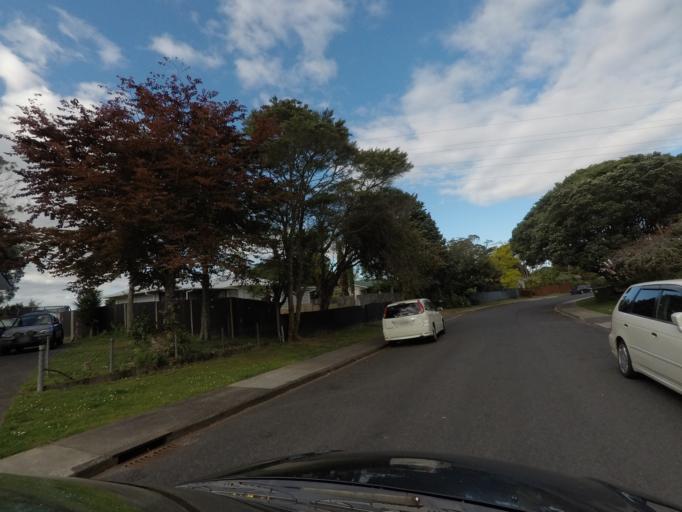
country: NZ
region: Auckland
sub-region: Auckland
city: Rosebank
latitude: -36.8819
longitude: 174.6579
